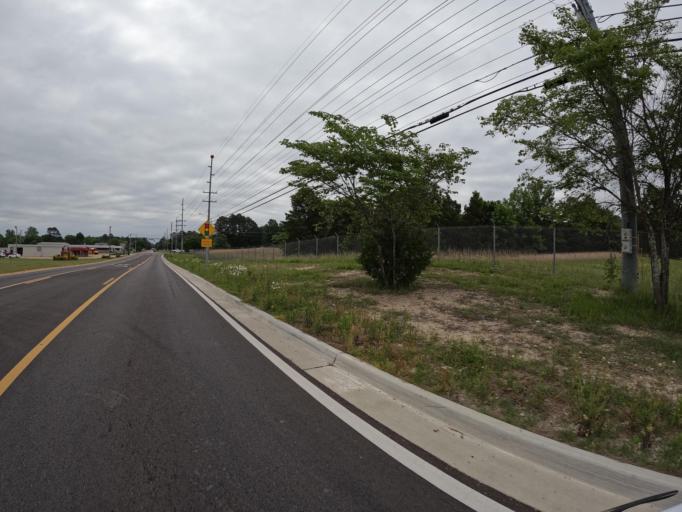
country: US
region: Mississippi
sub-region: Lee County
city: Tupelo
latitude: 34.2647
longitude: -88.7591
